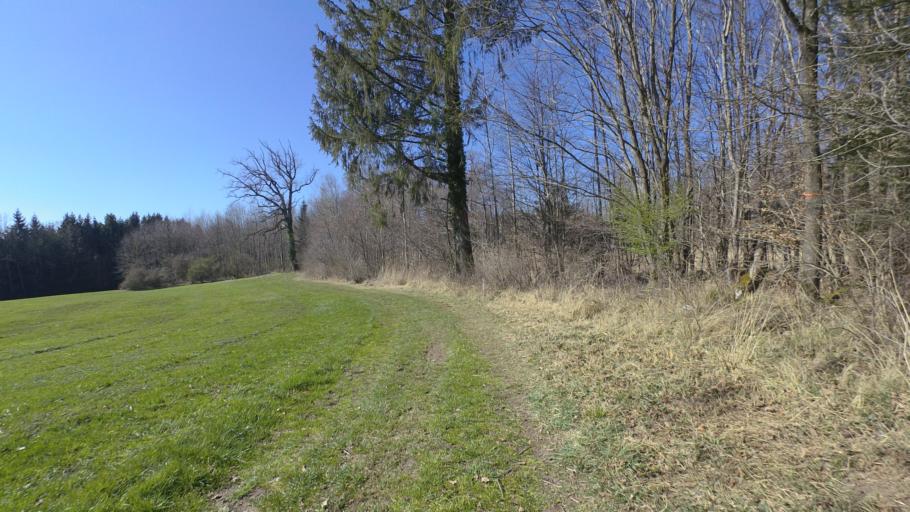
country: DE
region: Bavaria
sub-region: Upper Bavaria
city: Seeon-Seebruck
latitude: 47.9601
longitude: 12.4884
